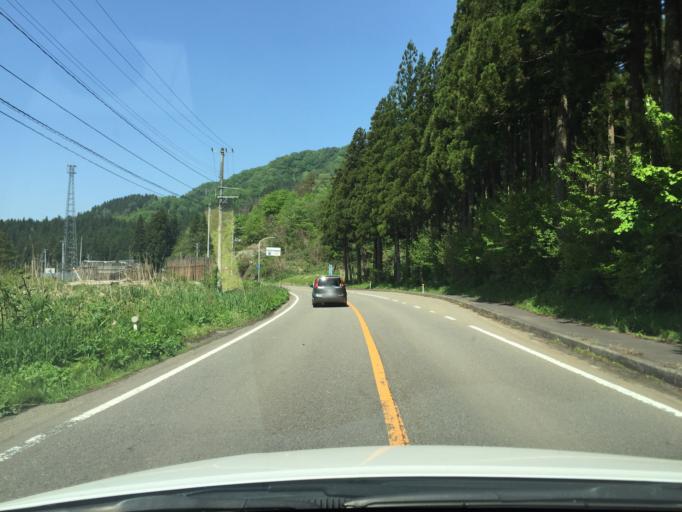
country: JP
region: Niigata
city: Muramatsu
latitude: 37.6429
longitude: 139.1179
